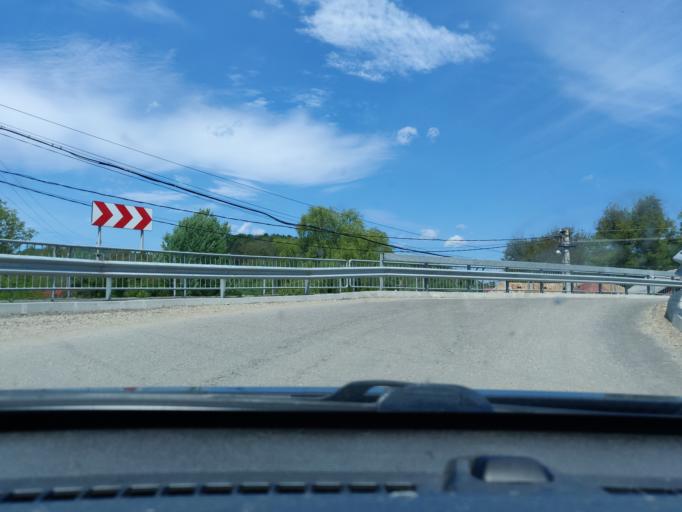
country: RO
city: Vizantea-Manastireasca
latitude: 45.9696
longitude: 26.8128
